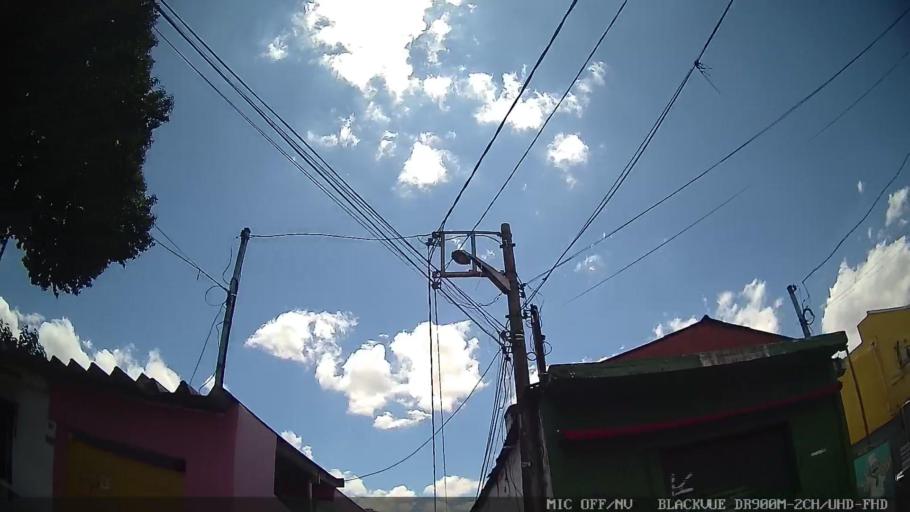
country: BR
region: Sao Paulo
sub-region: Diadema
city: Diadema
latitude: -23.6463
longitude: -46.6596
